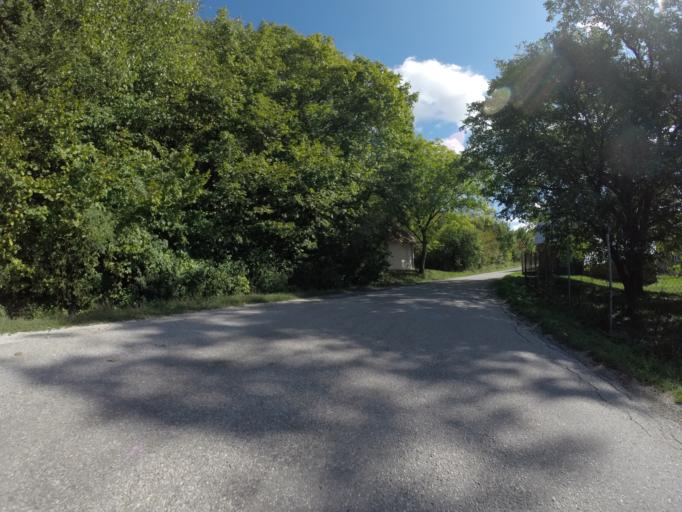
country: CZ
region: Zlin
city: Strani
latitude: 48.8362
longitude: 17.7381
